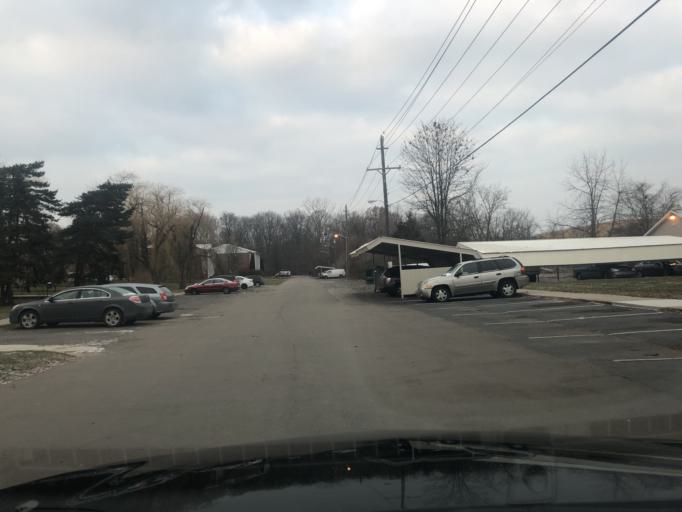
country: US
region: Michigan
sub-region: Wayne County
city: Romulus
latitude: 42.2315
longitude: -83.3875
